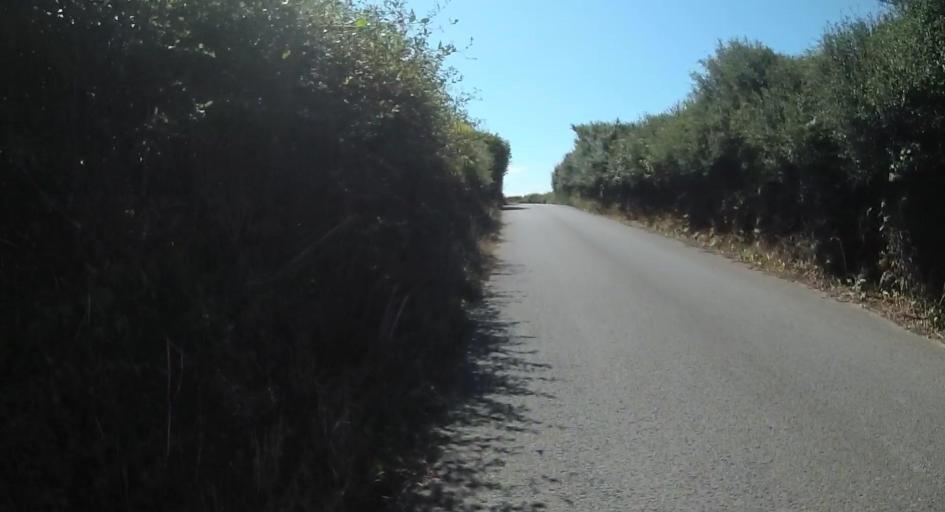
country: GB
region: England
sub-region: Isle of Wight
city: Chale
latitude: 50.6120
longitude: -1.3238
